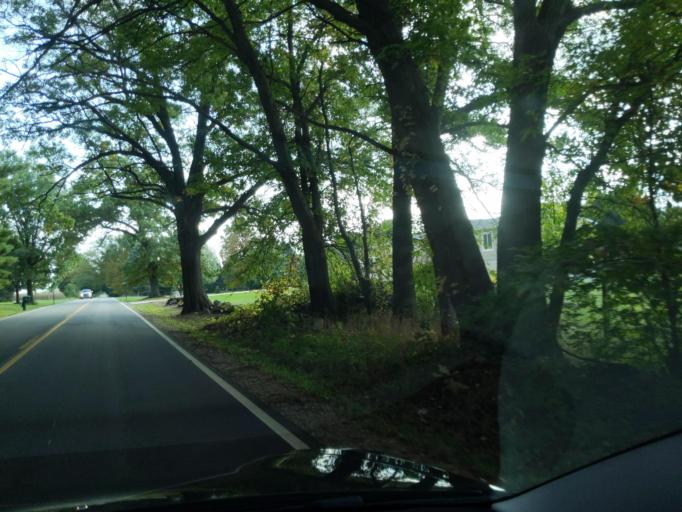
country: US
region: Michigan
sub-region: Ingham County
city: Leslie
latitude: 42.3770
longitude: -84.4432
